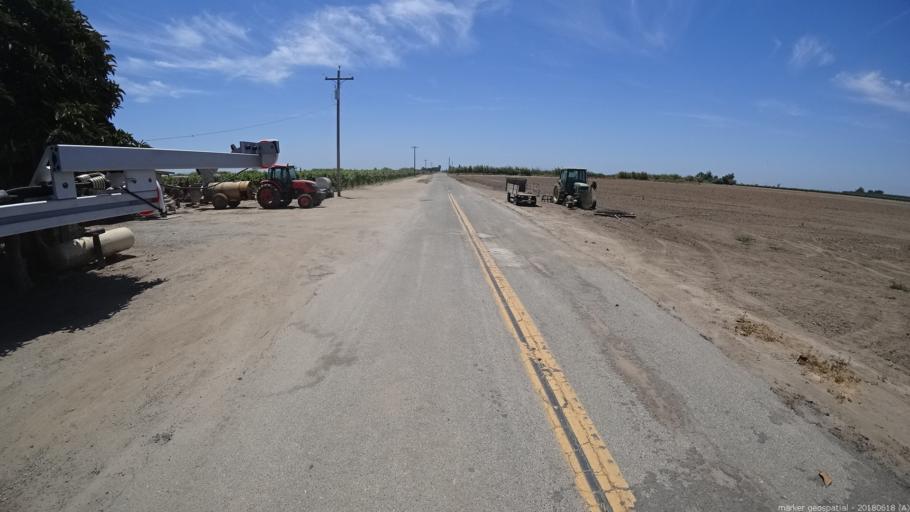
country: US
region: California
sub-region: Madera County
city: Parkwood
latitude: 36.9018
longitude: -120.1196
